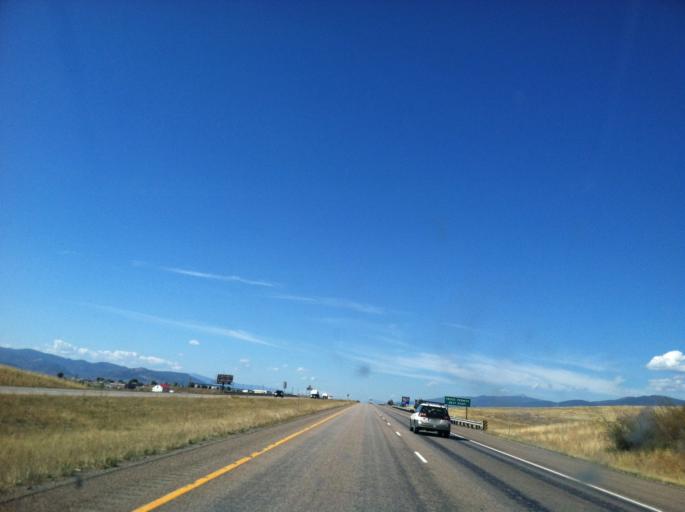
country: US
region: Montana
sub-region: Missoula County
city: Orchard Homes
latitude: 46.9429
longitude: -114.1163
